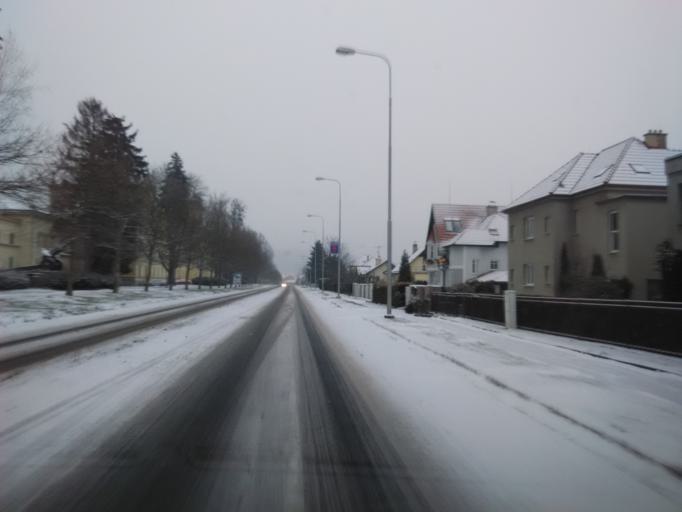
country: CZ
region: Olomoucky
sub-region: Okres Prerov
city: Hranice
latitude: 49.5510
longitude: 17.7200
